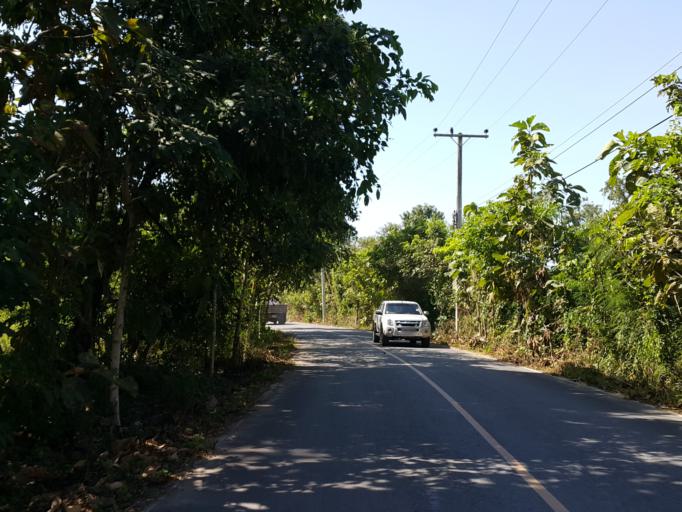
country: TH
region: Chiang Mai
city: Mae On
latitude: 18.8594
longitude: 99.1641
